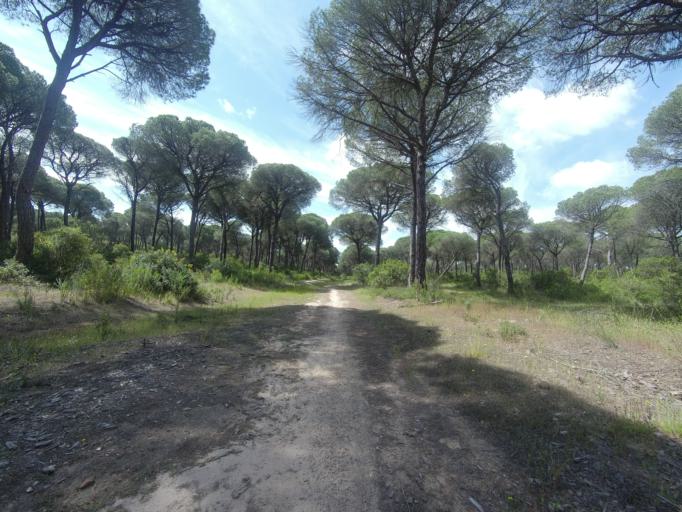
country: ES
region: Andalusia
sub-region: Provincia de Huelva
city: Aljaraque
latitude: 37.2273
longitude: -7.0675
